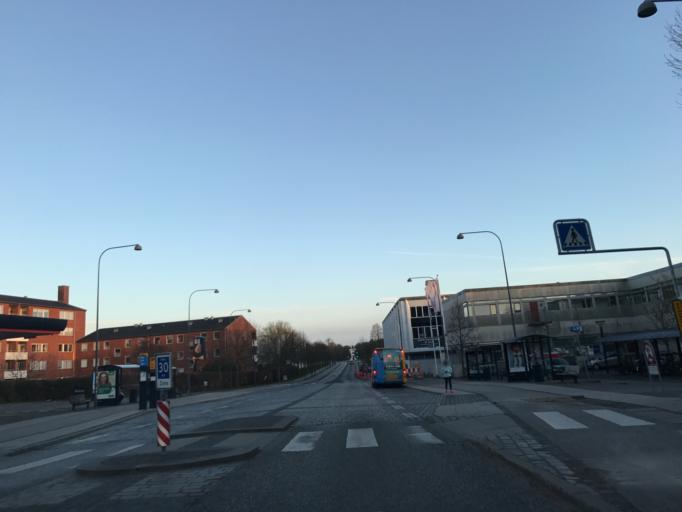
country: DK
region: Capital Region
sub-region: Horsholm Kommune
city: Horsholm
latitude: 55.8815
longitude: 12.4986
